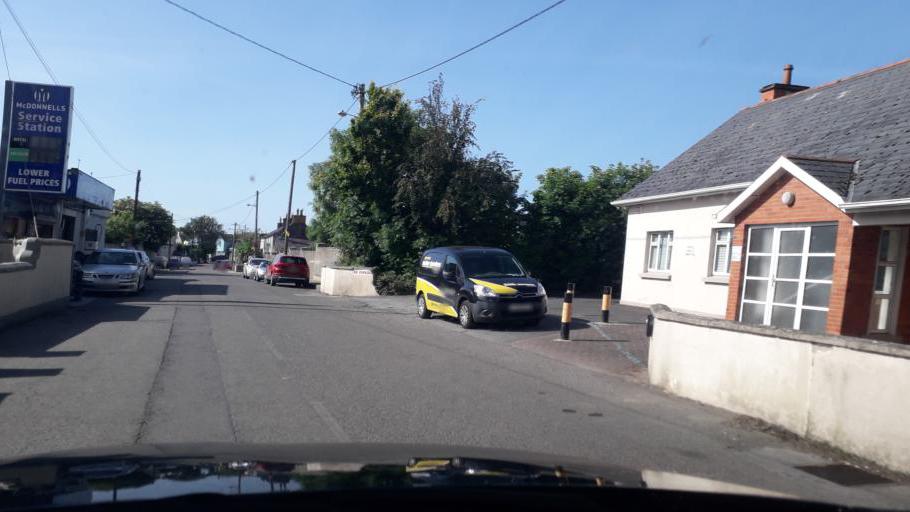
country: IE
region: Leinster
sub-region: Loch Garman
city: Loch Garman
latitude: 52.2325
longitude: -6.5531
